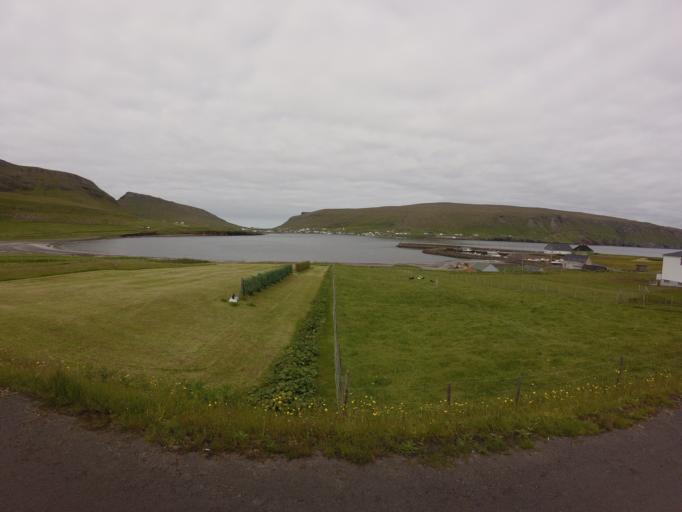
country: FO
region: Suduroy
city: Tvoroyri
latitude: 61.5917
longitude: -6.9315
